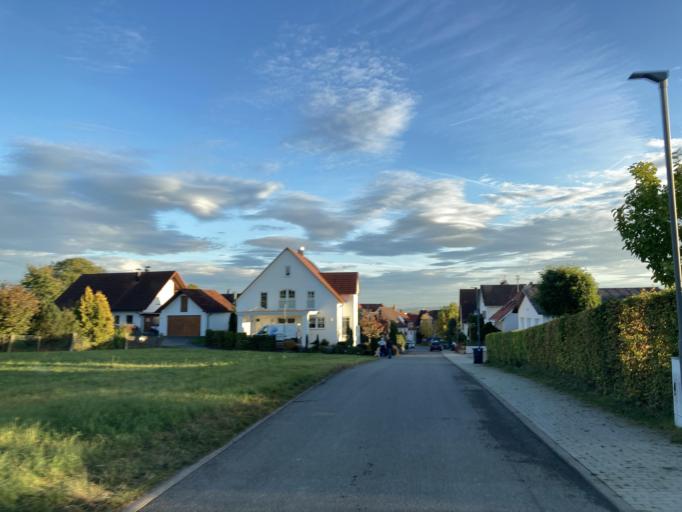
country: DE
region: Baden-Wuerttemberg
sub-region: Regierungsbezirk Stuttgart
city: Motzingen
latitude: 48.5082
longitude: 8.7708
